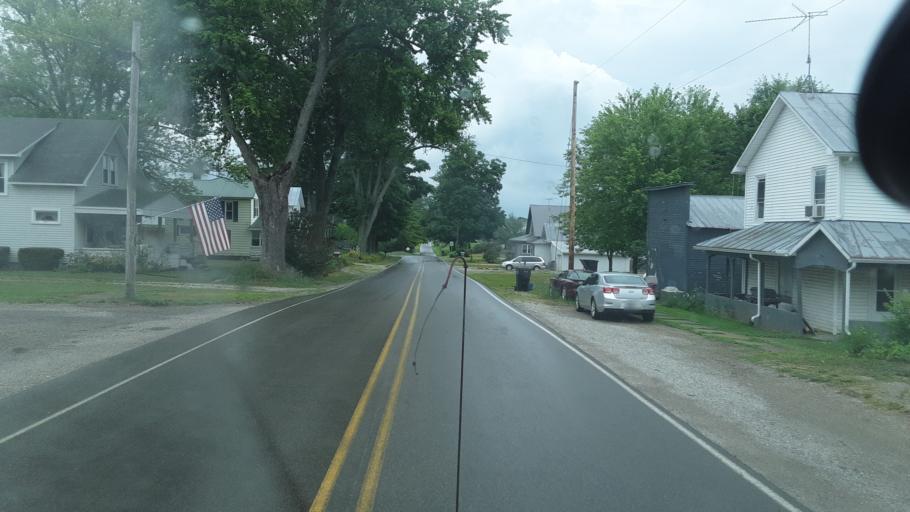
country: US
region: Indiana
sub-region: Steuben County
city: Hamilton
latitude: 41.6157
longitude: -84.8380
